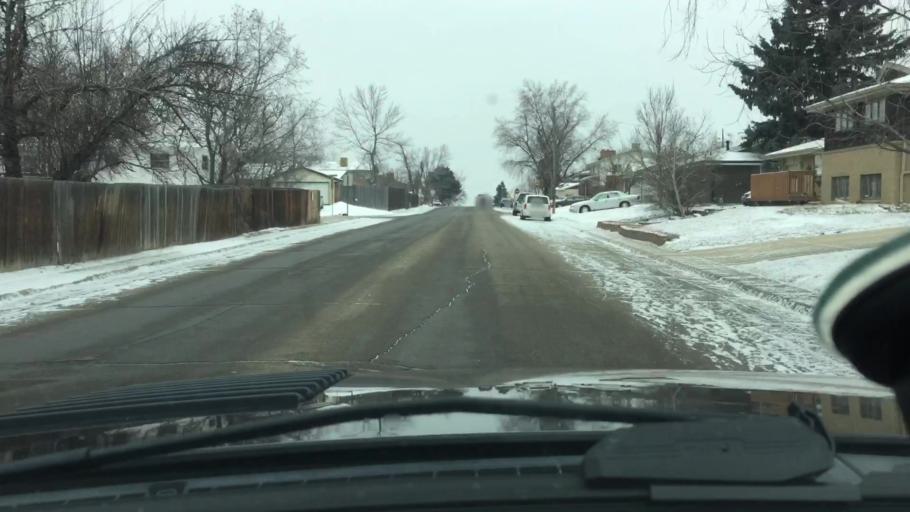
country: US
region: Colorado
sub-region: Adams County
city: Northglenn
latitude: 39.8800
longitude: -105.0056
